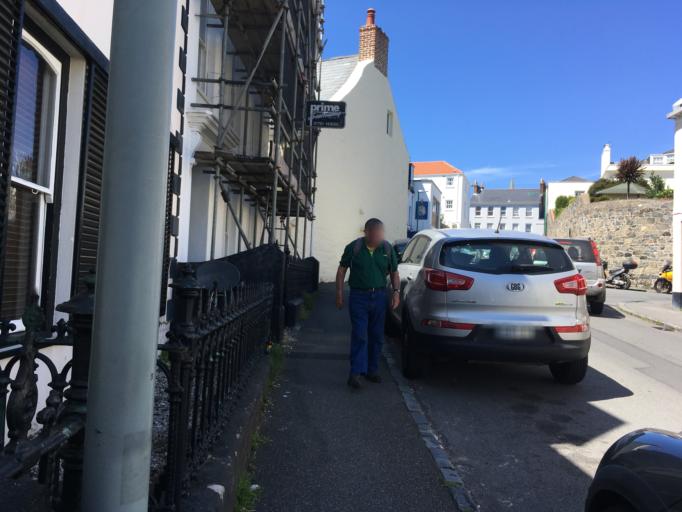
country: GG
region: St Peter Port
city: Saint Peter Port
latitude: 49.4550
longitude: -2.5468
